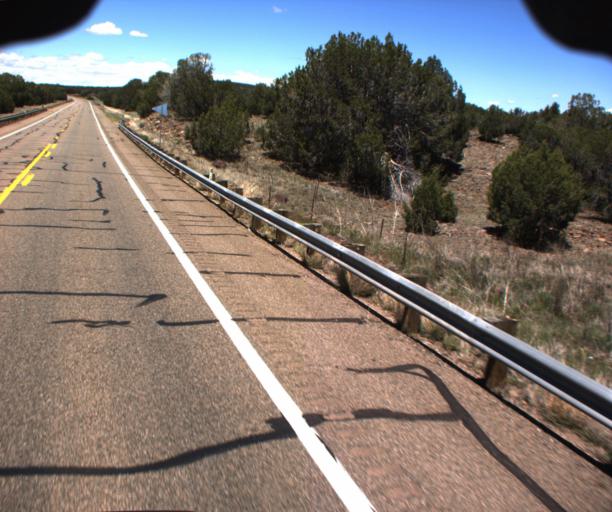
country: US
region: Arizona
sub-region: Yavapai County
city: Paulden
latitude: 35.1209
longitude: -112.4345
